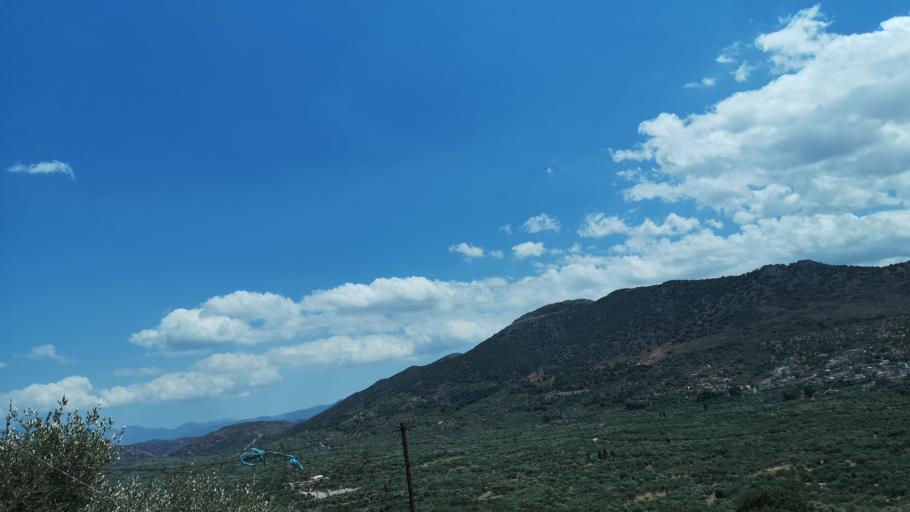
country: GR
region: Crete
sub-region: Nomos Lasithiou
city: Neapoli
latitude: 35.2512
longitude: 25.6296
